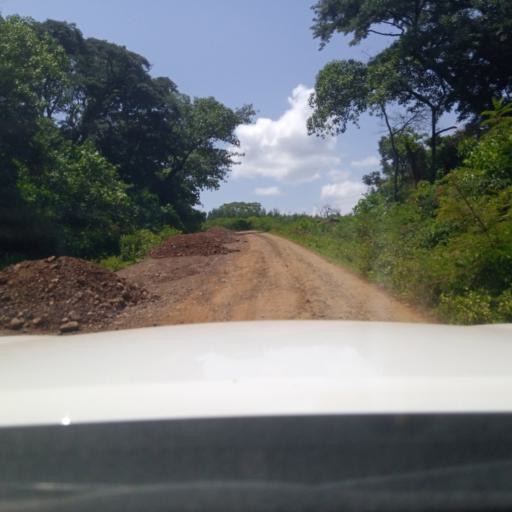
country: ET
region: Oromiya
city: Agaro
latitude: 8.1574
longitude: 36.9250
